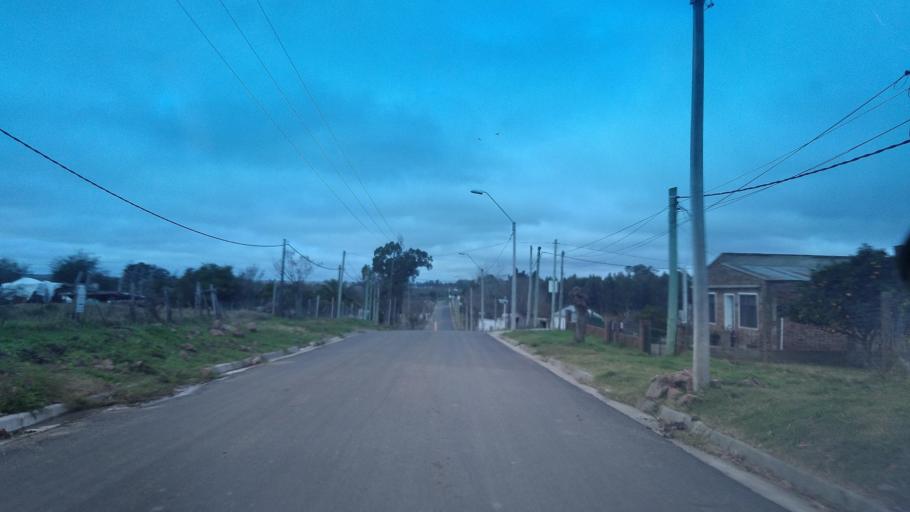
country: UY
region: Canelones
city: Tala
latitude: -34.2010
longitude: -55.7404
